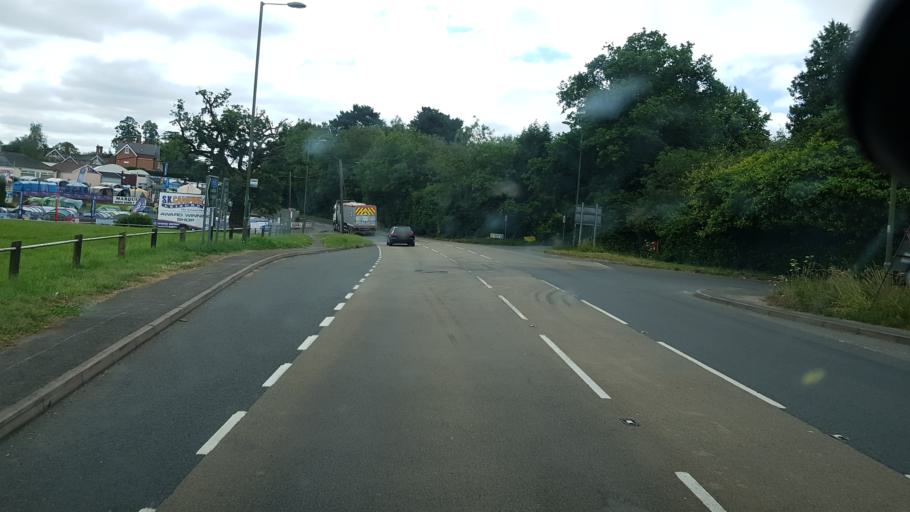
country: GB
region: England
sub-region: Surrey
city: Godstone
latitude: 51.2051
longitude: -0.0574
